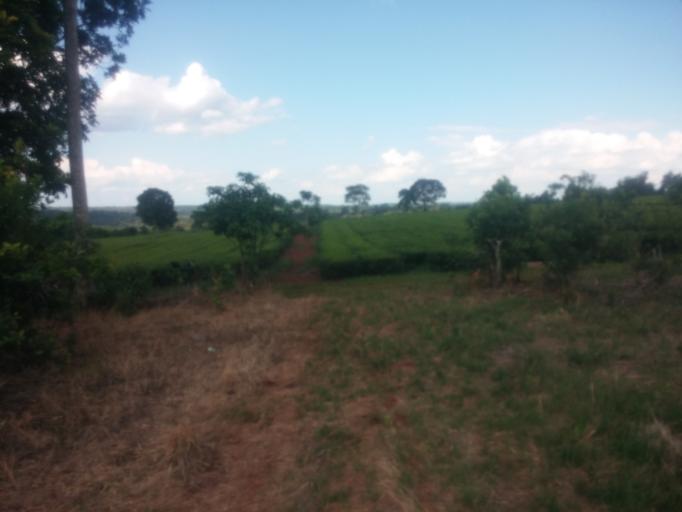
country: AR
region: Misiones
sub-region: Departamento de Obera
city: Obera
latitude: -27.4417
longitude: -55.0925
